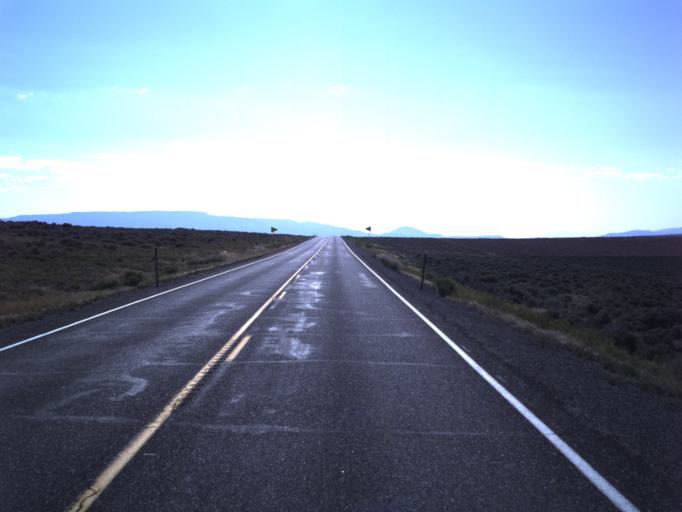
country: US
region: Utah
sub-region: Wayne County
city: Loa
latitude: 38.4434
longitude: -111.7942
